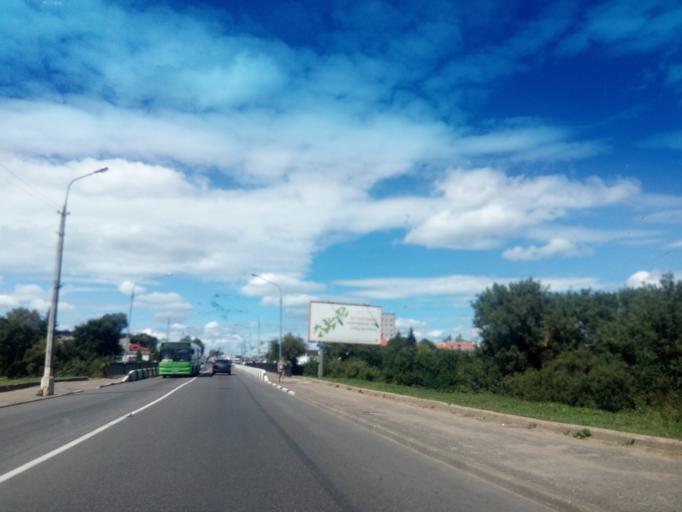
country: BY
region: Vitebsk
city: Polatsk
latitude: 55.4932
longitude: 28.7726
